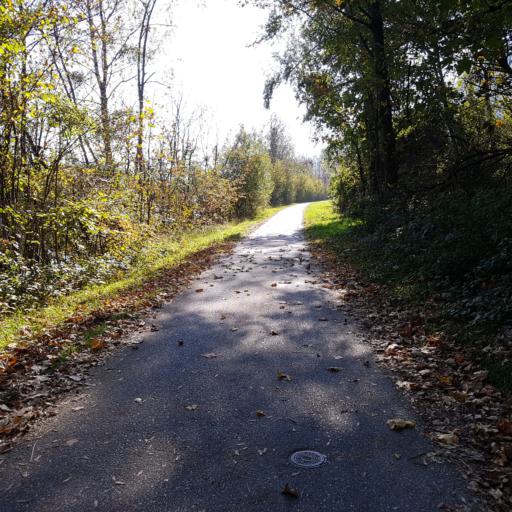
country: AT
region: Salzburg
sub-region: Politischer Bezirk Hallein
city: Oberalm
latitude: 47.6964
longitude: 13.0805
